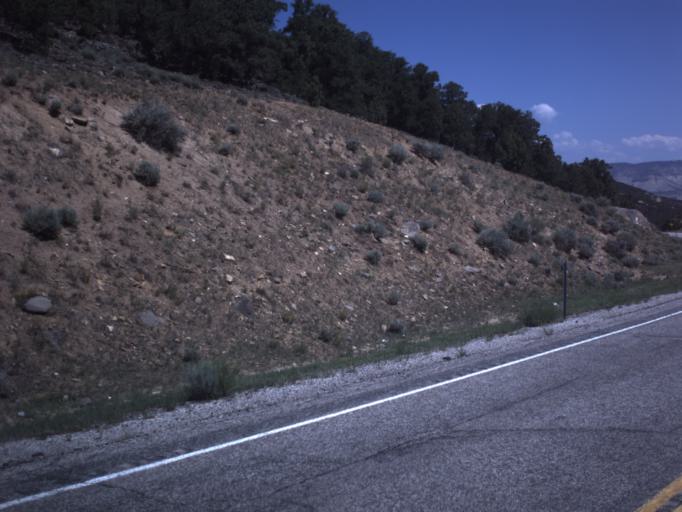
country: US
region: Utah
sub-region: Wayne County
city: Loa
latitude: 38.7186
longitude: -111.3983
